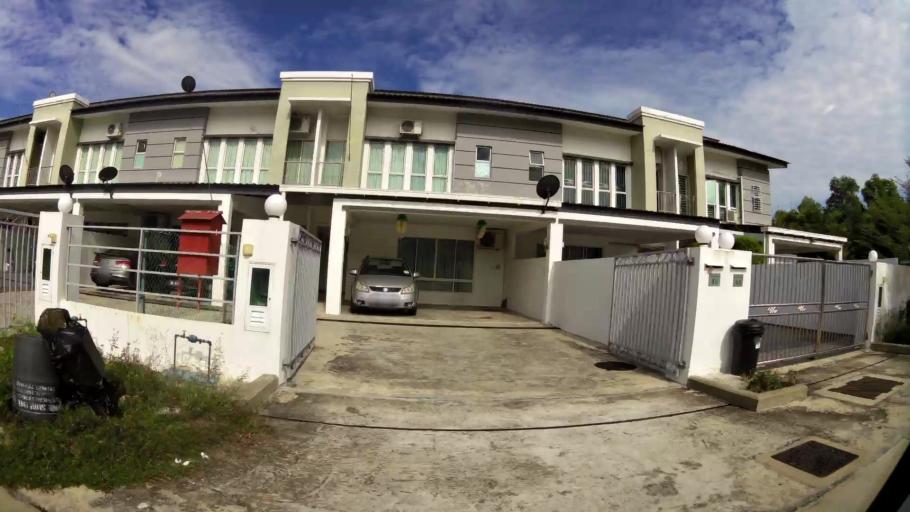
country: BN
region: Brunei and Muara
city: Bandar Seri Begawan
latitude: 4.9257
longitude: 114.8984
